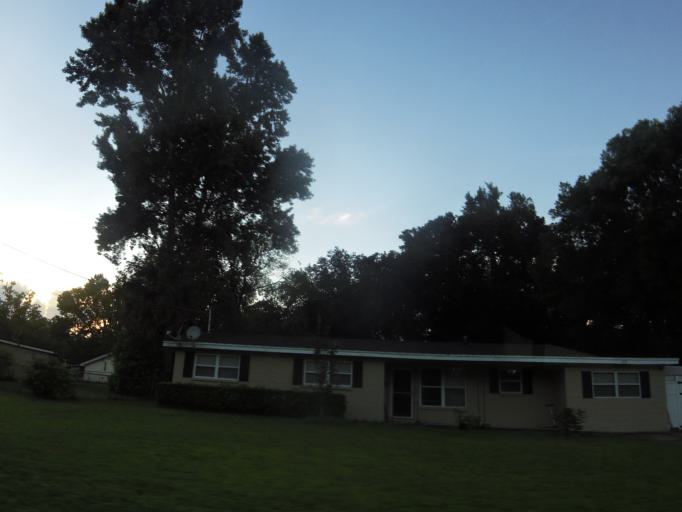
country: US
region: Florida
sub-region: Duval County
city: Jacksonville
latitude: 30.2324
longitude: -81.6088
